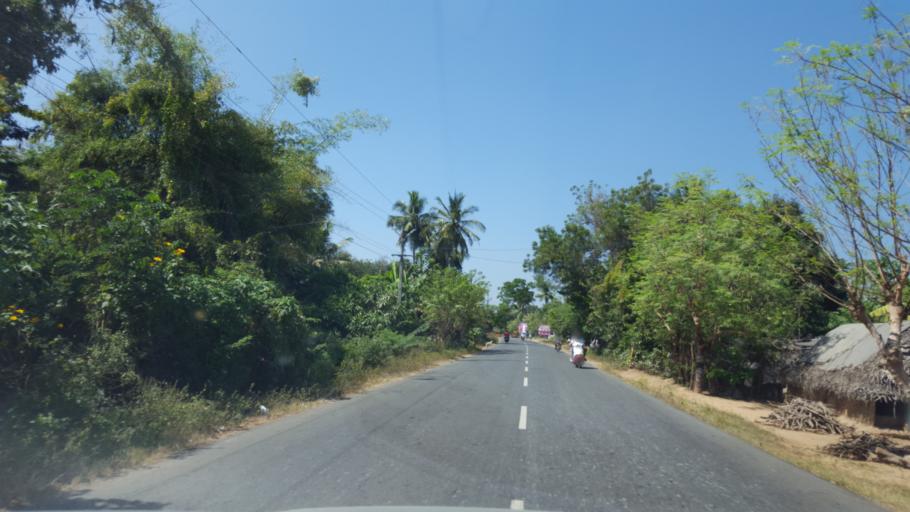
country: IN
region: Tamil Nadu
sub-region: Kancheepuram
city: Chengalpattu
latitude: 12.7265
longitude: 79.9507
